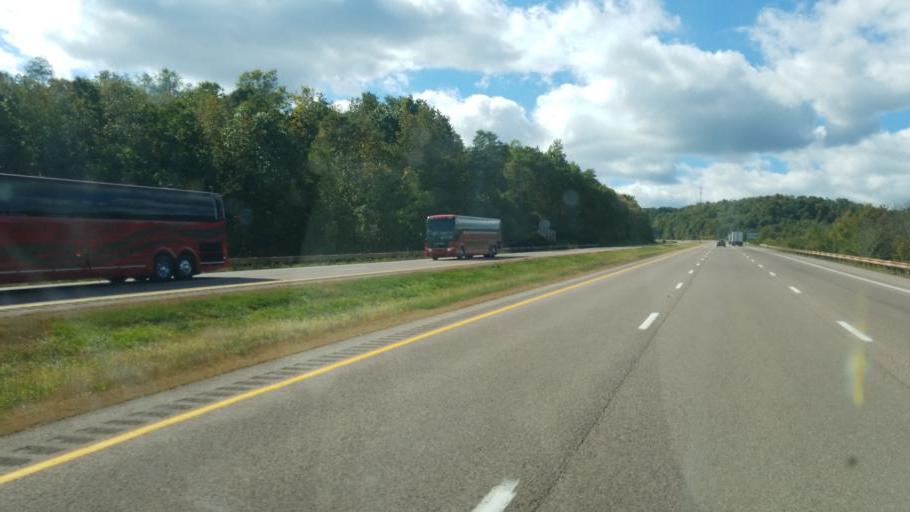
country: US
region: West Virginia
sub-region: Preston County
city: Terra Alta
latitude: 39.6618
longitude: -79.4668
